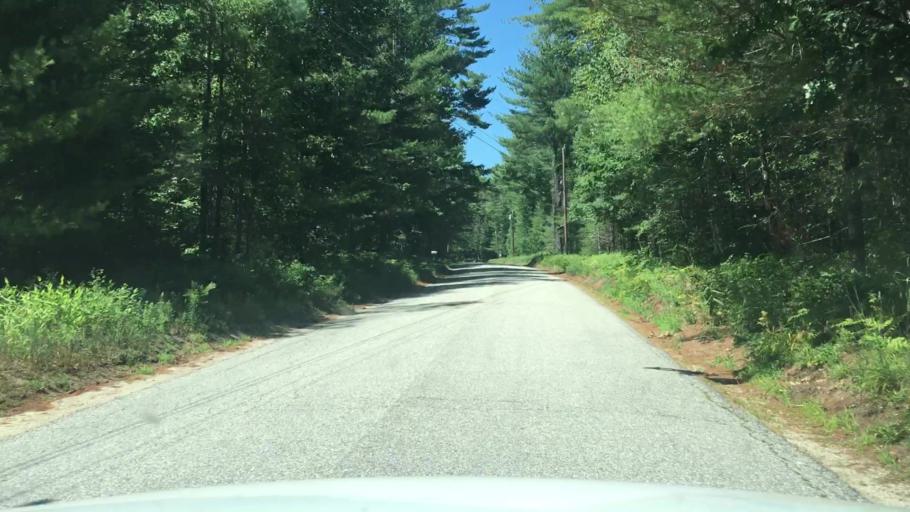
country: US
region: New Hampshire
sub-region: Merrimack County
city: Hopkinton
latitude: 43.2315
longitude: -71.6529
